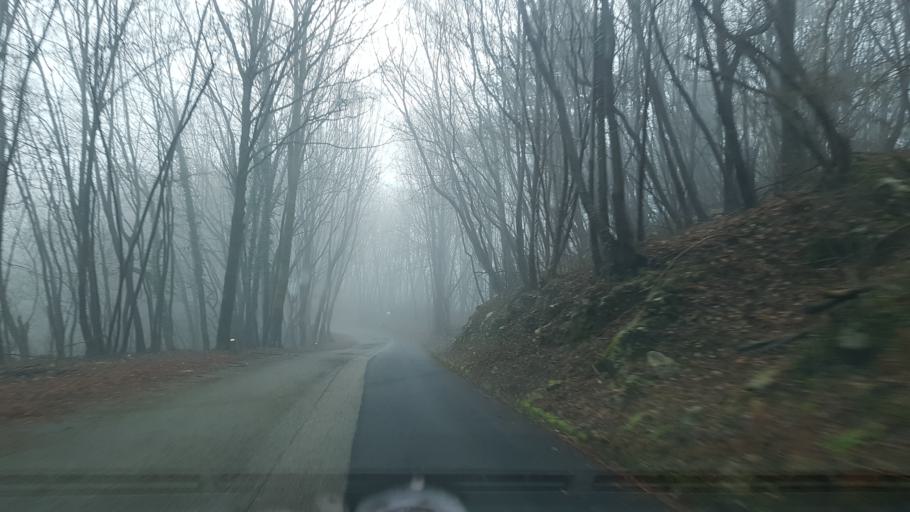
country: IT
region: Friuli Venezia Giulia
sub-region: Provincia di Udine
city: Stregna
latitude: 46.1098
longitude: 13.5805
